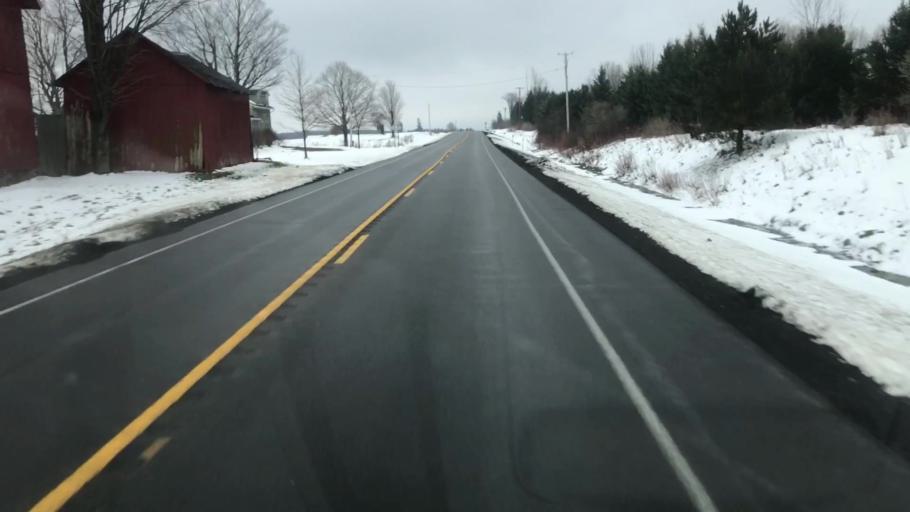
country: US
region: New York
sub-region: Cayuga County
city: Moravia
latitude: 42.7676
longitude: -76.3319
